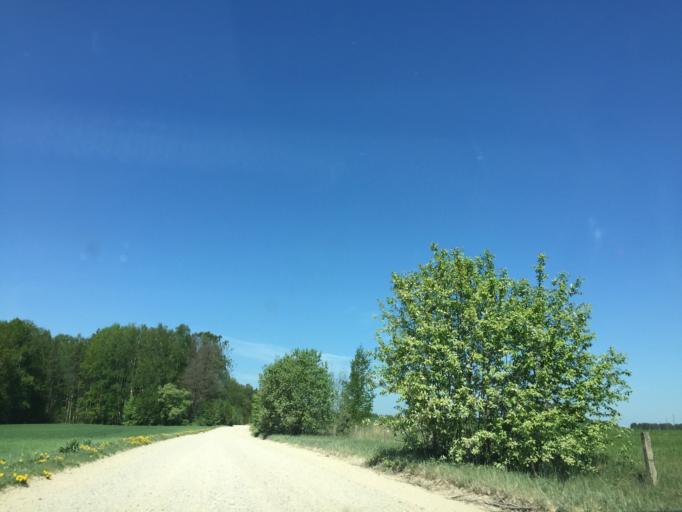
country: LV
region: Ikskile
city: Ikskile
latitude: 56.8753
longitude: 24.4978
